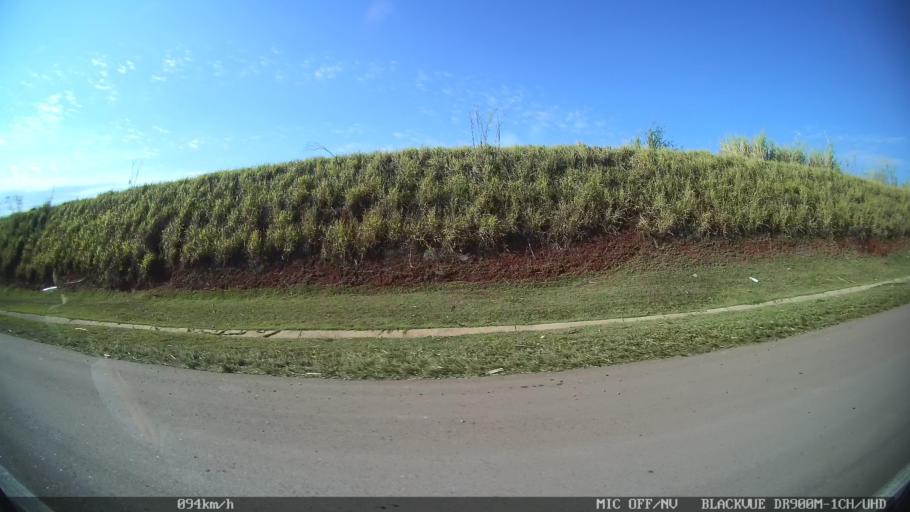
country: BR
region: Sao Paulo
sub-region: Piracicaba
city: Piracicaba
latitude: -22.7122
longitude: -47.6091
